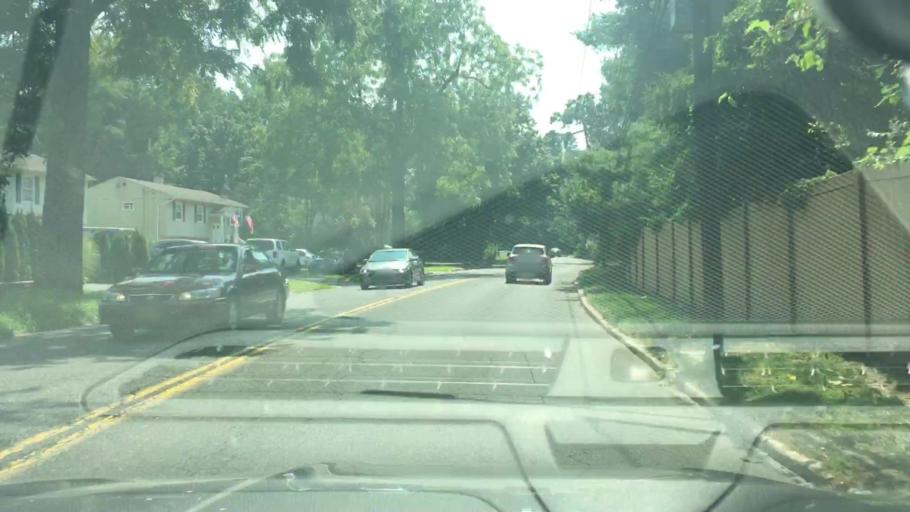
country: US
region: New York
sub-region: Suffolk County
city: Hauppauge
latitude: 40.8223
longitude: -73.2342
